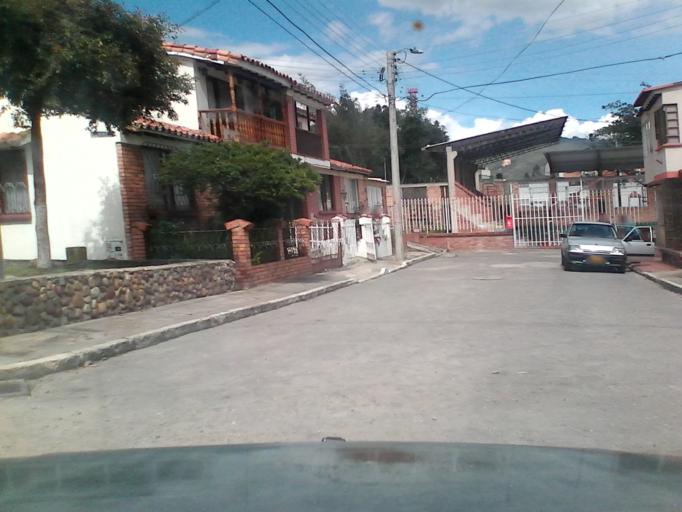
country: CO
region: Boyaca
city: Duitama
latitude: 5.8353
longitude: -73.0359
